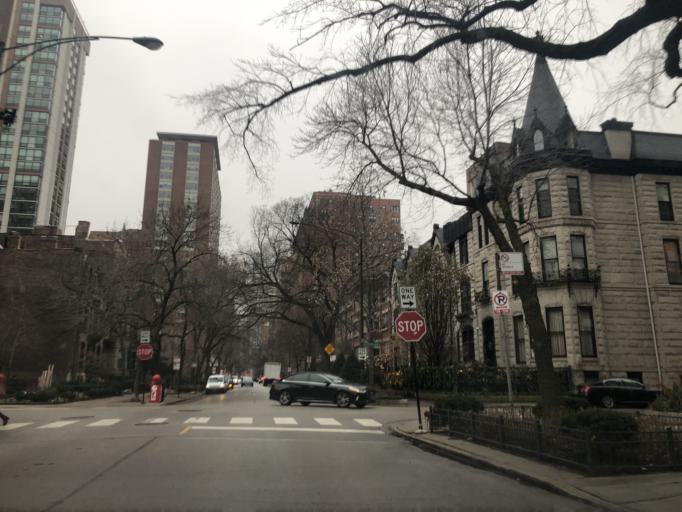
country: US
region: Illinois
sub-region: Cook County
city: Chicago
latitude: 41.9081
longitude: -87.6287
